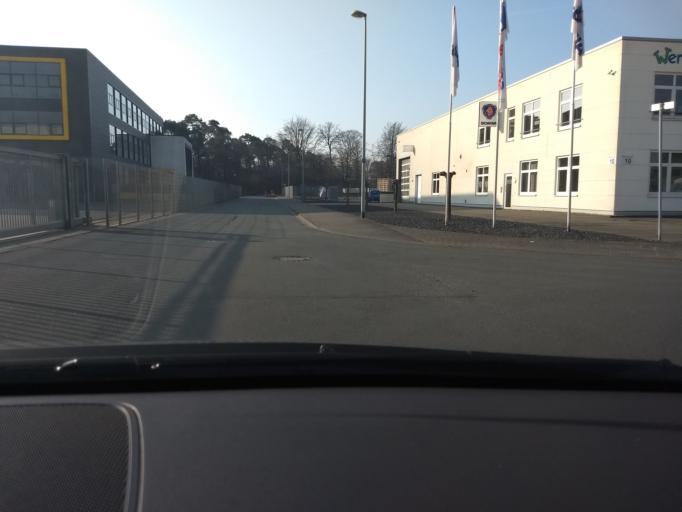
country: DE
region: North Rhine-Westphalia
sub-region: Regierungsbezirk Munster
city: Rhede
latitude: 51.8305
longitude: 6.7200
